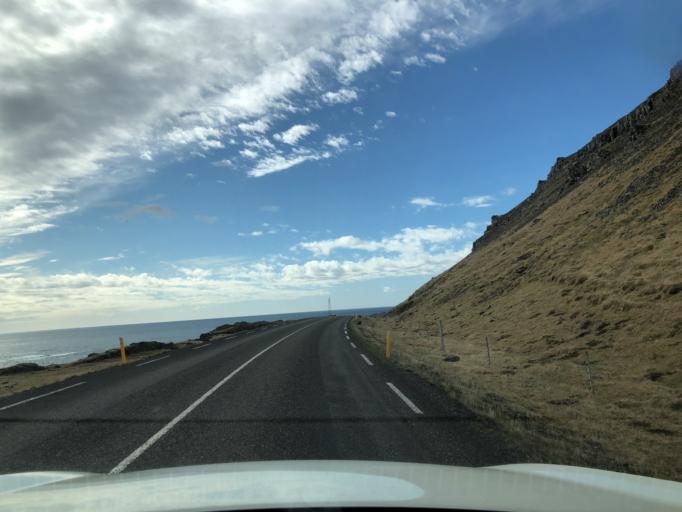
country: IS
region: East
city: Eskifjoerdur
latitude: 64.7368
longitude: -13.9902
